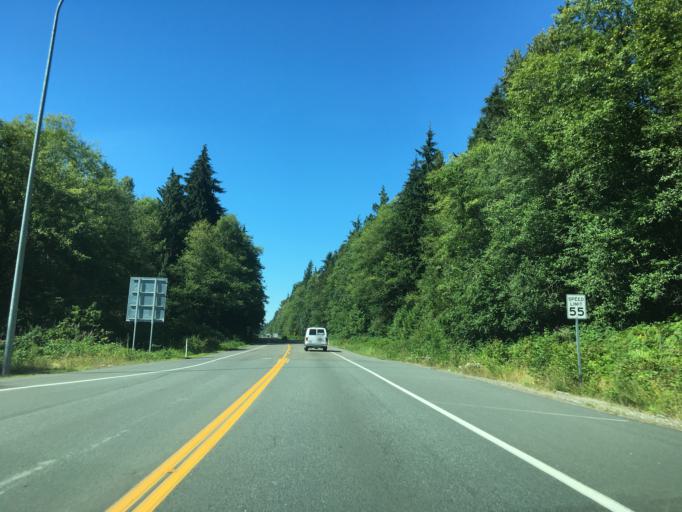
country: US
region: Washington
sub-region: Snohomish County
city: Sisco Heights
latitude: 48.1537
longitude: -122.1137
